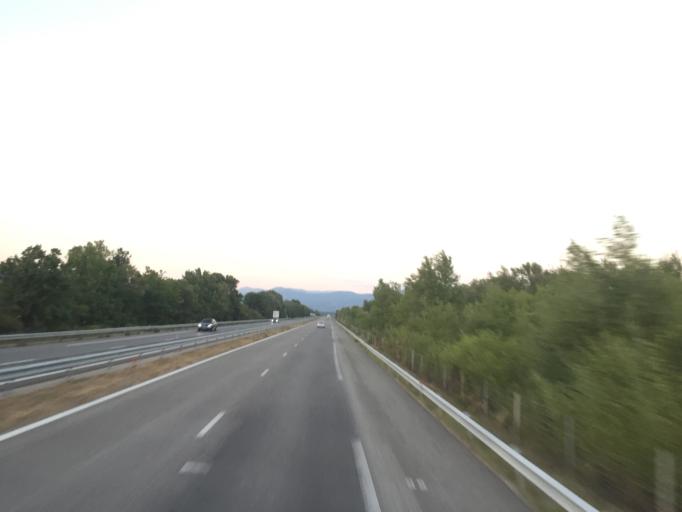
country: FR
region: Provence-Alpes-Cote d'Azur
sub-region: Departement des Alpes-de-Haute-Provence
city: Peyruis
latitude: 44.0125
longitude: 5.9369
